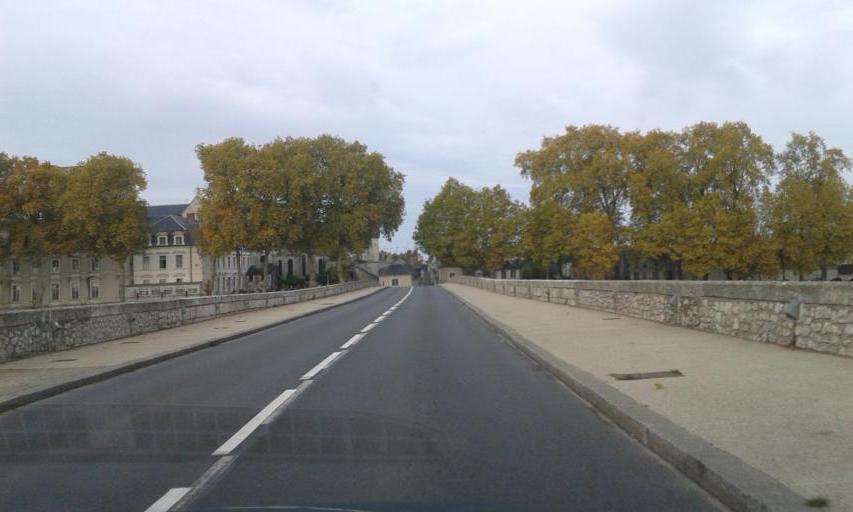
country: FR
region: Centre
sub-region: Departement du Loiret
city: Beaugency
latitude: 47.7768
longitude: 1.6369
